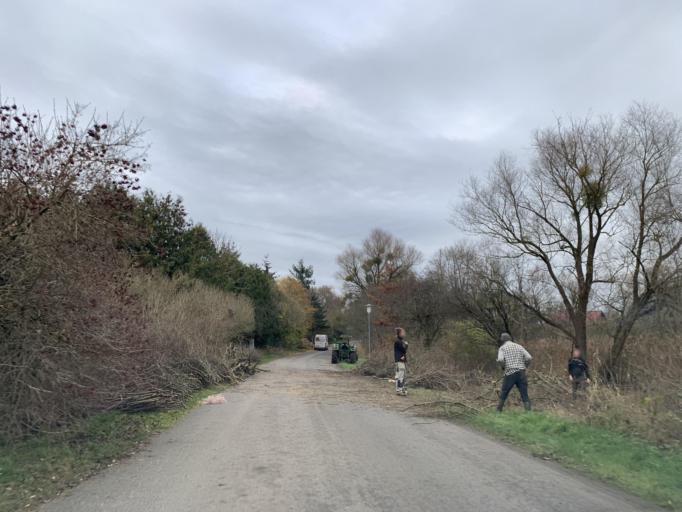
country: DE
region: Mecklenburg-Vorpommern
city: Carpin
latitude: 53.4040
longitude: 13.2004
